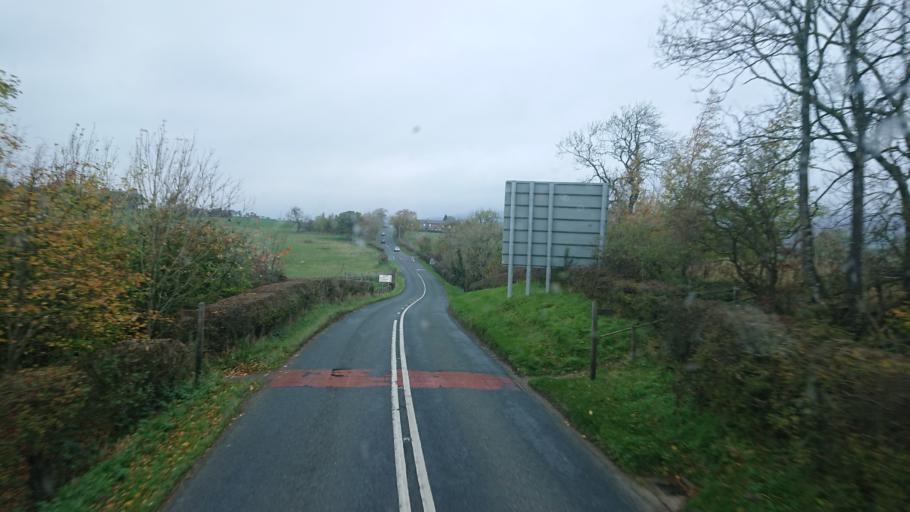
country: GB
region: England
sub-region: North Yorkshire
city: Skipton
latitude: 53.9727
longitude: -2.0271
